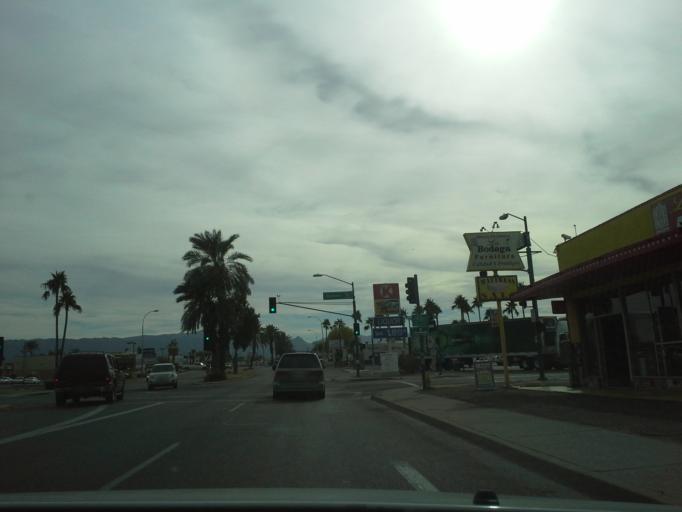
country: US
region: Arizona
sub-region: Maricopa County
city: Phoenix
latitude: 33.3996
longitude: -112.0734
